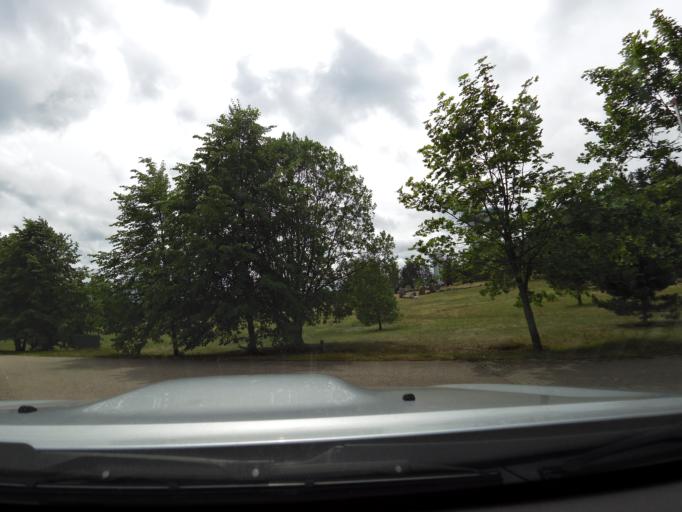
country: LT
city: Moletai
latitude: 55.3170
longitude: 25.5564
